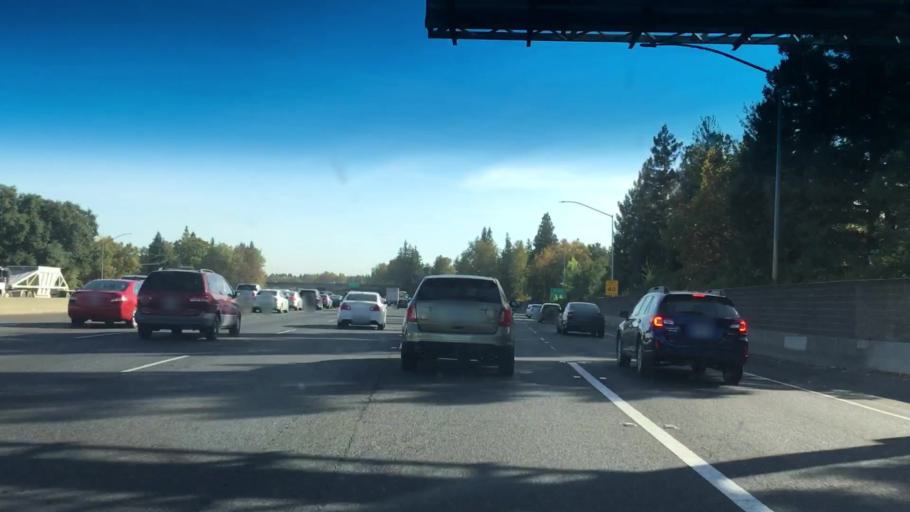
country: US
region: California
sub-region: Sacramento County
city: Parkway
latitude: 38.5002
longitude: -121.5177
